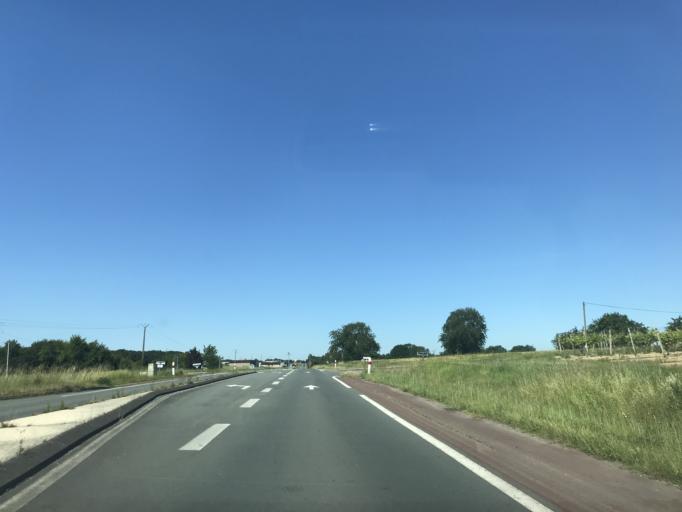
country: FR
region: Poitou-Charentes
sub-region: Departement de la Charente-Maritime
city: Pons
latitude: 45.5733
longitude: -0.5745
